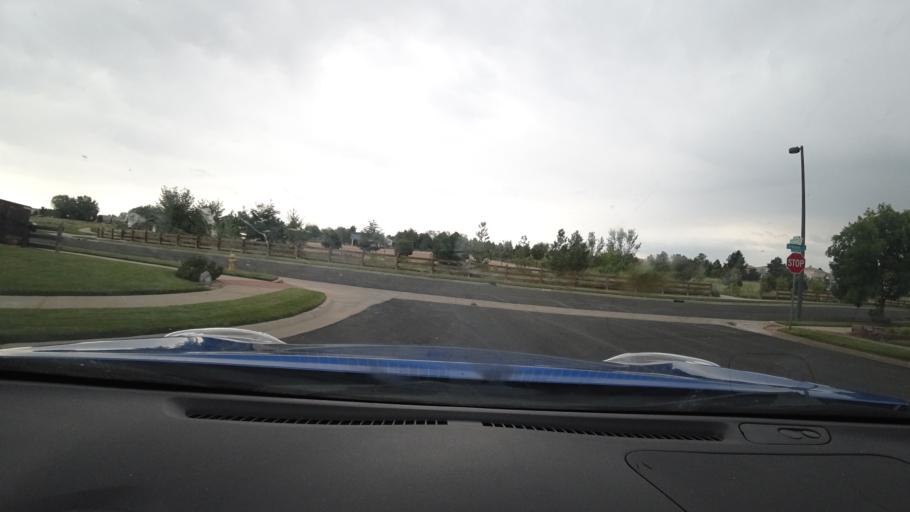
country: US
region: Colorado
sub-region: Adams County
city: Aurora
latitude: 39.7799
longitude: -104.7520
